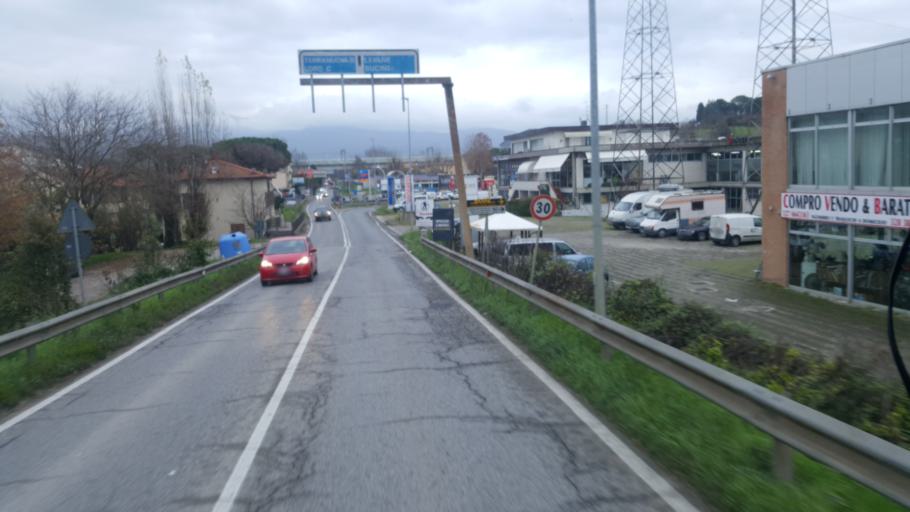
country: IT
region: Tuscany
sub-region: Province of Arezzo
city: Terranuova Bracciolini
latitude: 43.5425
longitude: 11.5683
